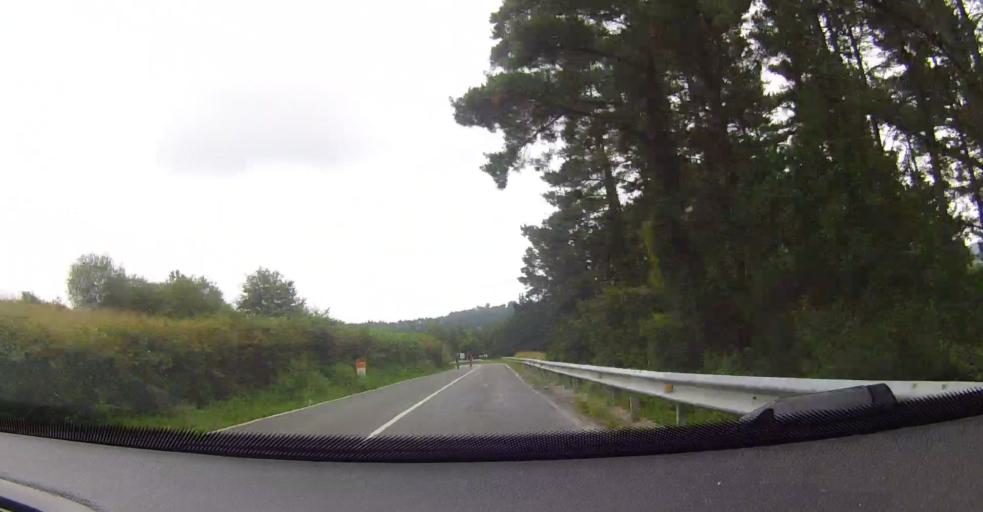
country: ES
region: Basque Country
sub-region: Bizkaia
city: Balmaseda
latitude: 43.2432
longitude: -3.2346
